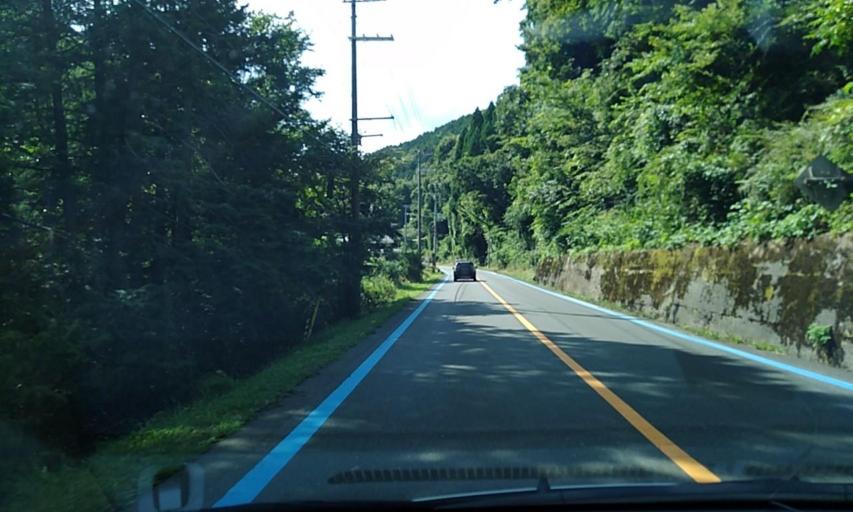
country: JP
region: Kyoto
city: Ayabe
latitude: 35.3071
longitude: 135.2929
